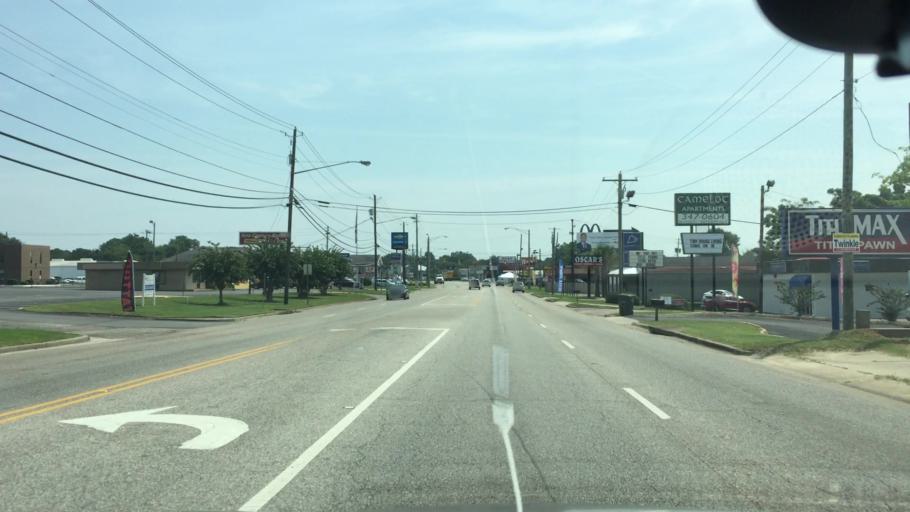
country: US
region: Alabama
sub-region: Coffee County
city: Enterprise
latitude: 31.3237
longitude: -85.8280
